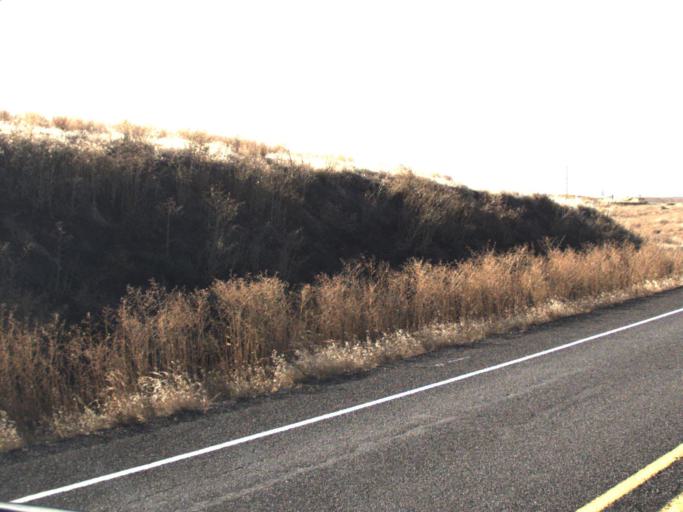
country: US
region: Washington
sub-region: Walla Walla County
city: Garrett
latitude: 46.2958
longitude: -118.5632
